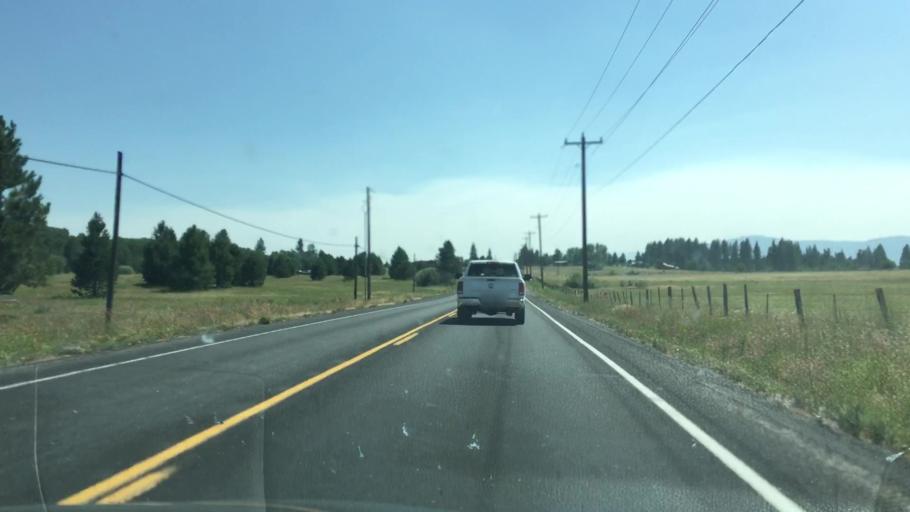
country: US
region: Idaho
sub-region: Valley County
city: McCall
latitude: 44.8794
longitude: -116.0907
